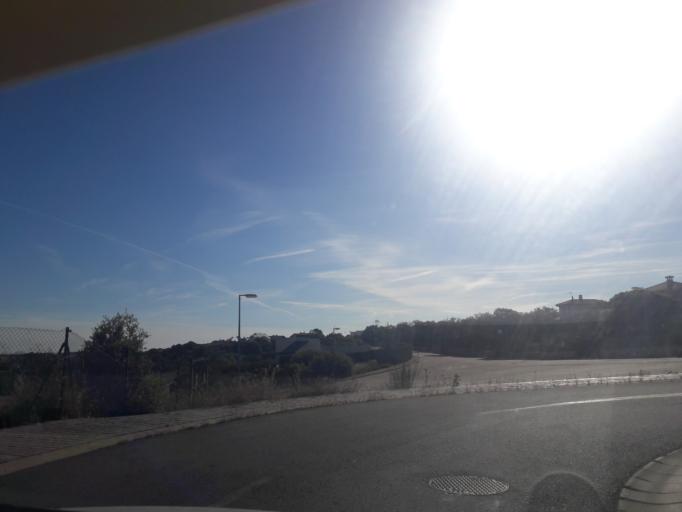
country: ES
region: Castille and Leon
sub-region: Provincia de Salamanca
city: Martinamor
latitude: 40.8082
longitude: -5.6452
